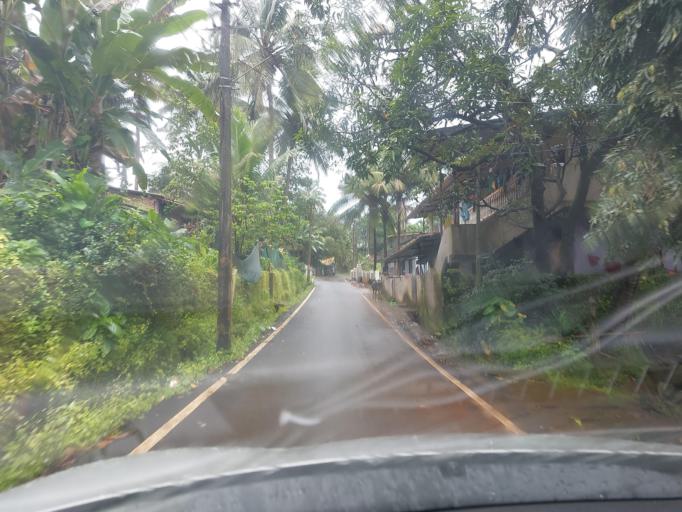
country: IN
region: Goa
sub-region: North Goa
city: Valpoy
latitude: 15.5317
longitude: 74.1293
